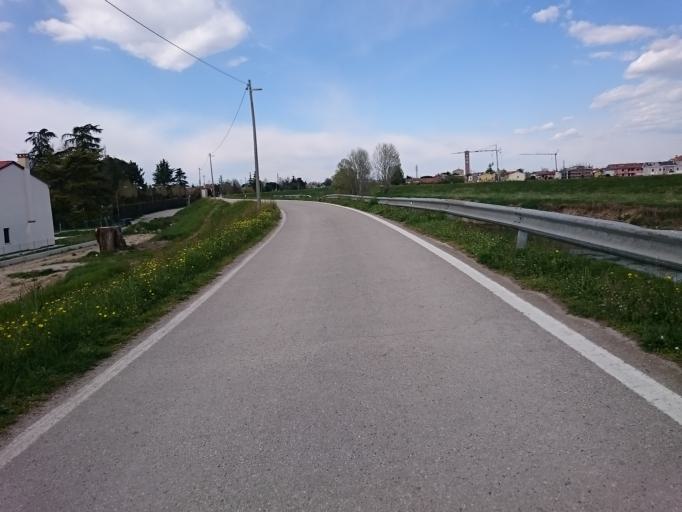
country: IT
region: Veneto
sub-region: Provincia di Padova
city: Ponte San Nicolo
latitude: 45.3590
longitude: 11.9341
